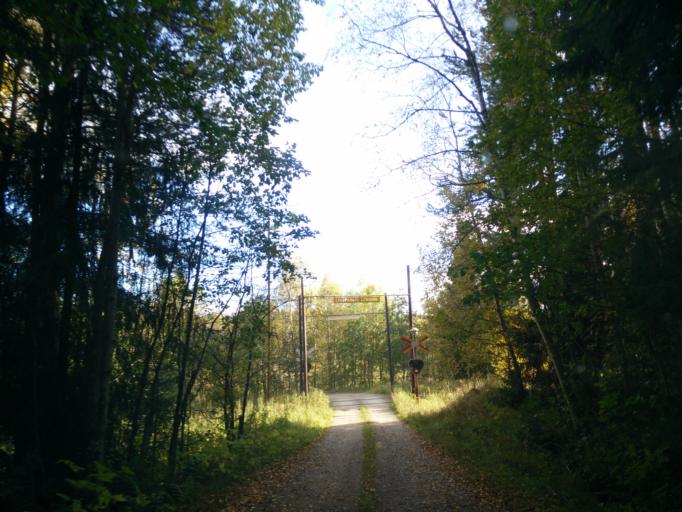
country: SE
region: Vaesternorrland
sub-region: Sundsvalls Kommun
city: Matfors
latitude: 62.3663
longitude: 17.0883
